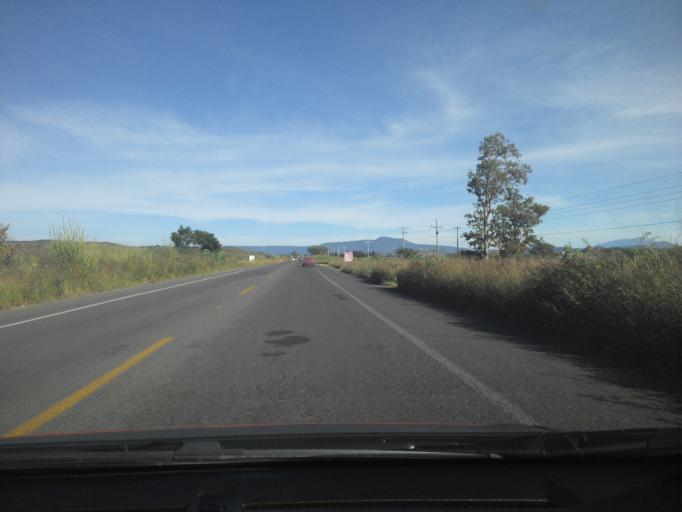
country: MX
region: Jalisco
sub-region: Teuchitlan
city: La Estanzuela
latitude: 20.6706
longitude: -103.8097
